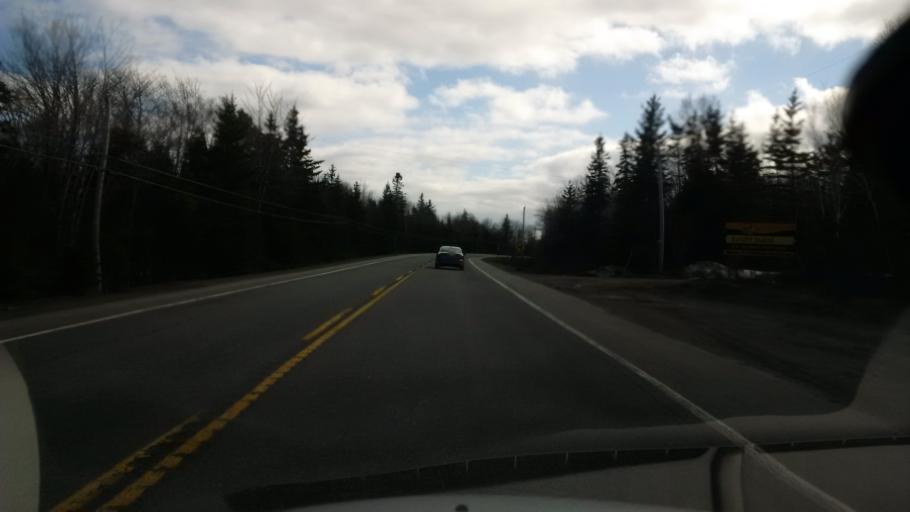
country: CA
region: Nova Scotia
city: Princeville
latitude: 46.0038
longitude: -60.9984
